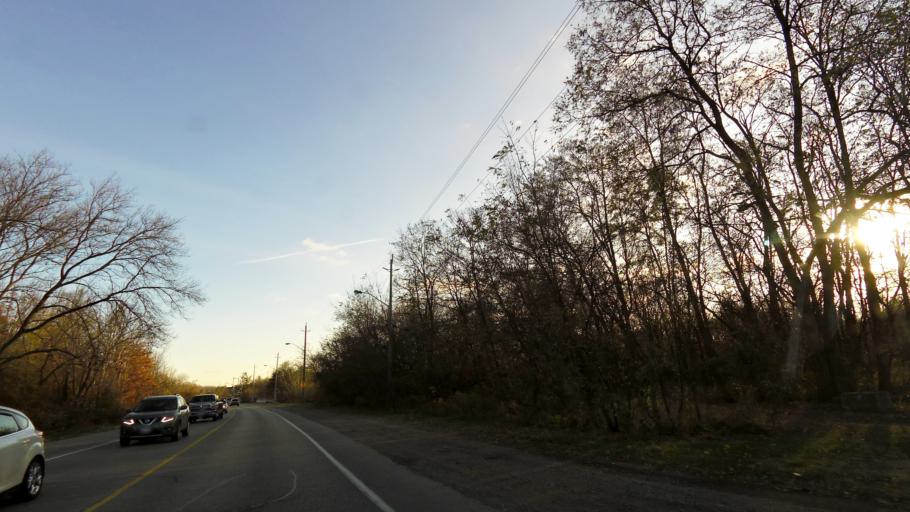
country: CA
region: Ontario
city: Cambridge
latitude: 43.3445
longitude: -80.3148
